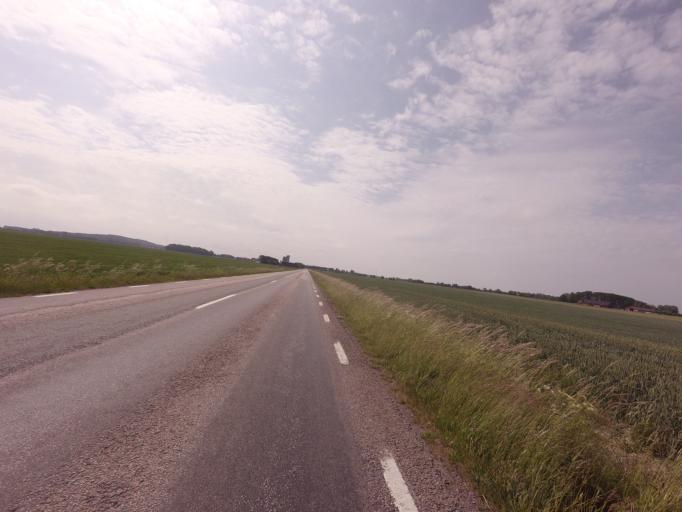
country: SE
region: Skane
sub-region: Helsingborg
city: Odakra
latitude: 56.1881
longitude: 12.6759
